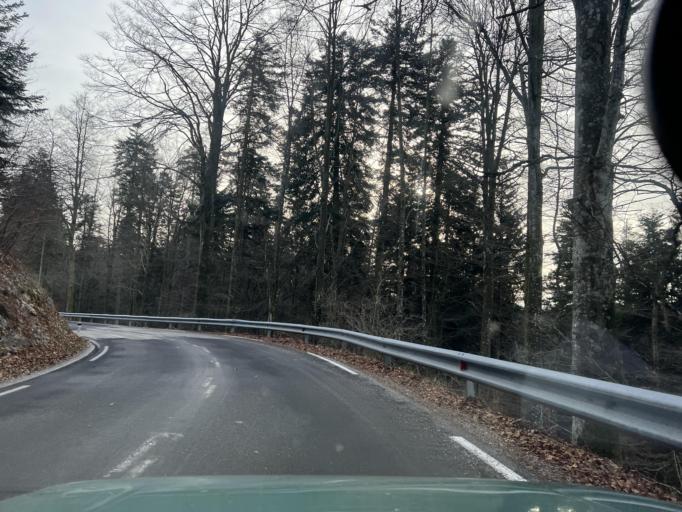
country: SI
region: Nova Gorica
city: Sempas
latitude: 46.0069
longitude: 13.7821
